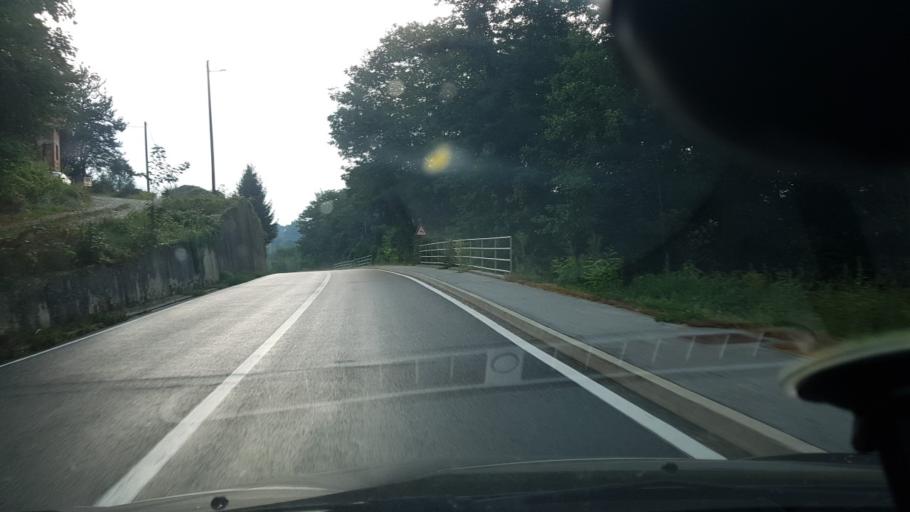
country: HR
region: Krapinsko-Zagorska
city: Pregrada
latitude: 46.2070
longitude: 15.7598
